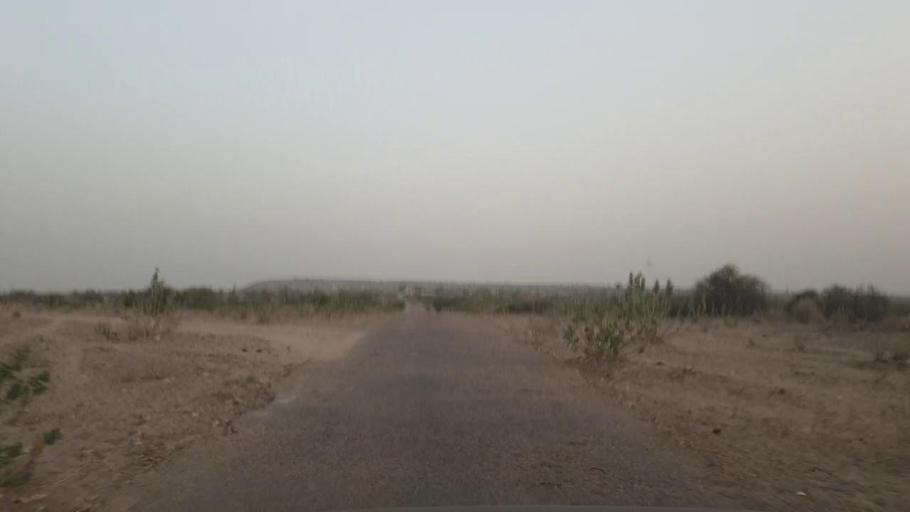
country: PK
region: Sindh
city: Chor
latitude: 25.5050
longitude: 69.8198
